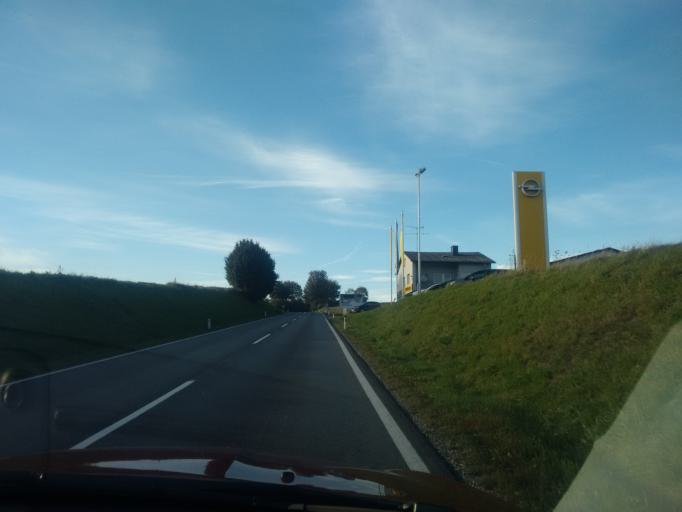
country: AT
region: Upper Austria
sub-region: Politischer Bezirk Vocklabruck
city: Niederthalheim
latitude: 48.1483
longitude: 13.7339
